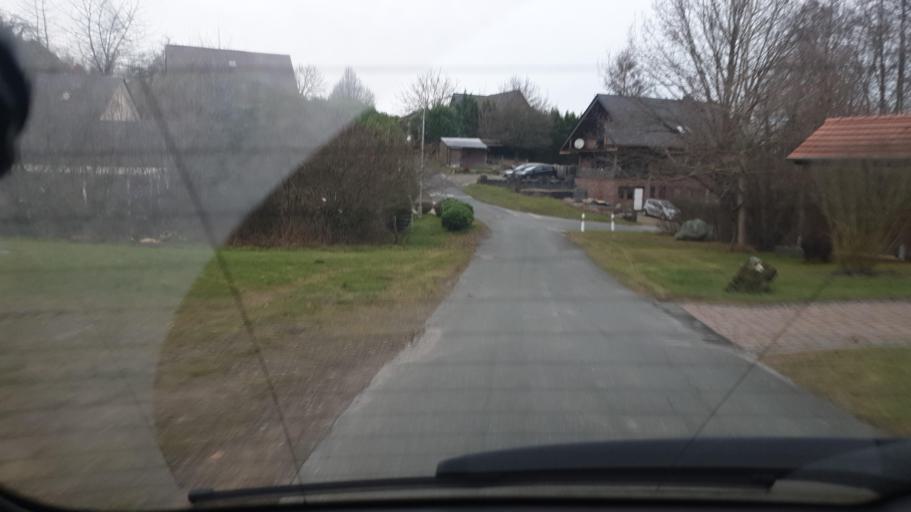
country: DE
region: North Rhine-Westphalia
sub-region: Regierungsbezirk Detmold
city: Hille
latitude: 52.2818
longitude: 8.7512
